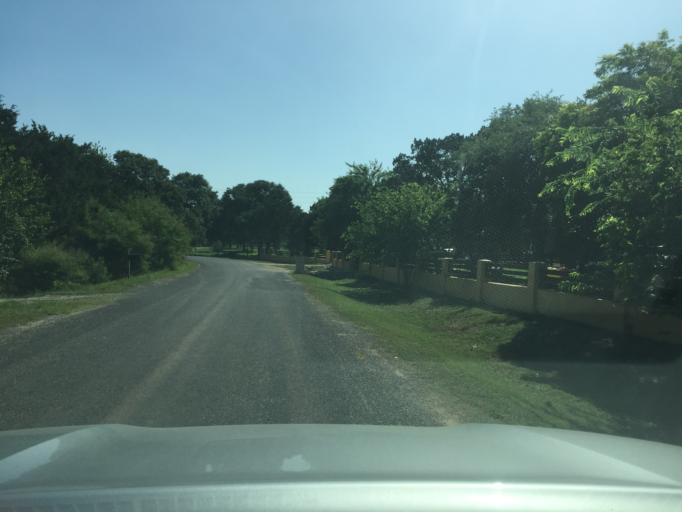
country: US
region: Texas
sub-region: Bexar County
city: Timberwood Park
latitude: 29.7060
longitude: -98.4775
